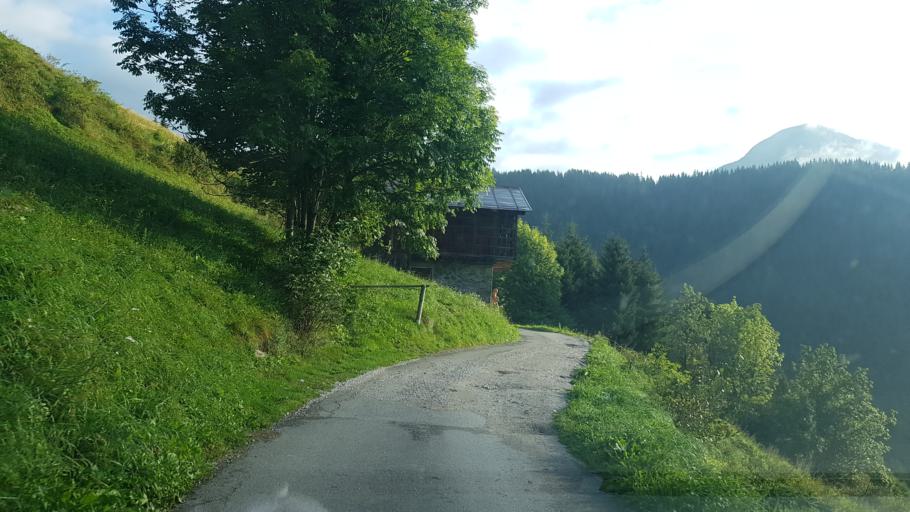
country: IT
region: Veneto
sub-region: Provincia di Belluno
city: San Pietro di Cadore
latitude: 46.5842
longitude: 12.5802
